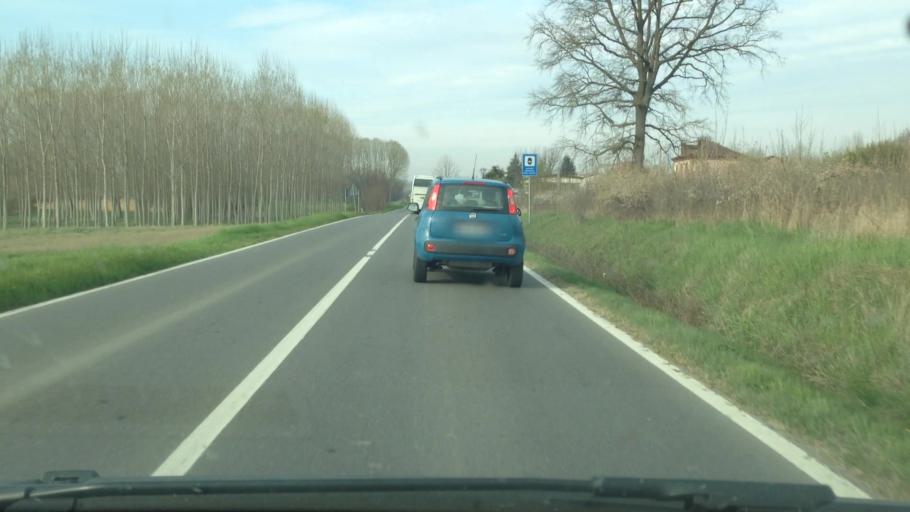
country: IT
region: Piedmont
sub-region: Provincia di Asti
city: Celle Enomondo
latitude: 44.8542
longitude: 8.0963
